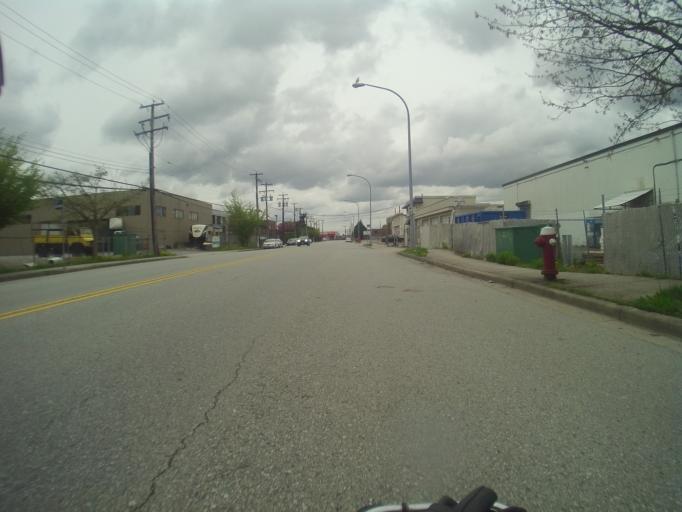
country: CA
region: British Columbia
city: Richmond
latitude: 49.1939
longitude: -123.0874
